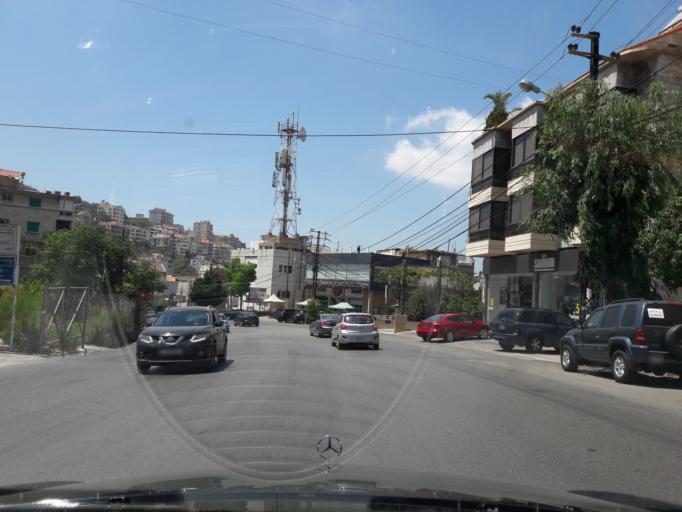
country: LB
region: Mont-Liban
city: Djounie
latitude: 33.9267
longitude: 35.6355
